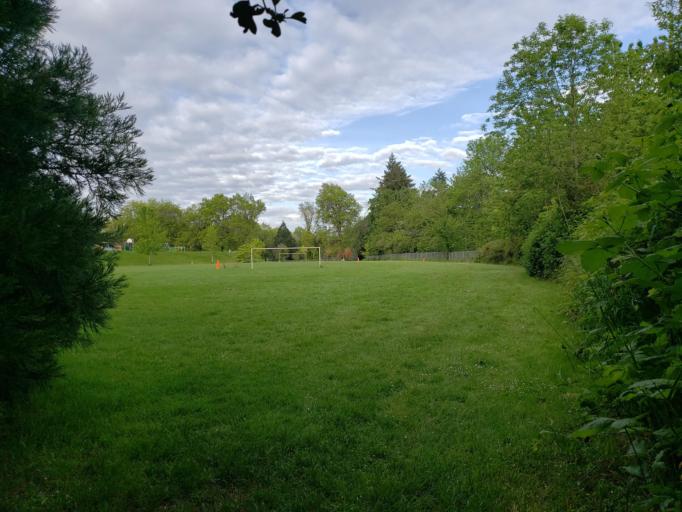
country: US
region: Oregon
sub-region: Washington County
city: Raleigh Hills
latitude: 45.4814
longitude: -122.7284
